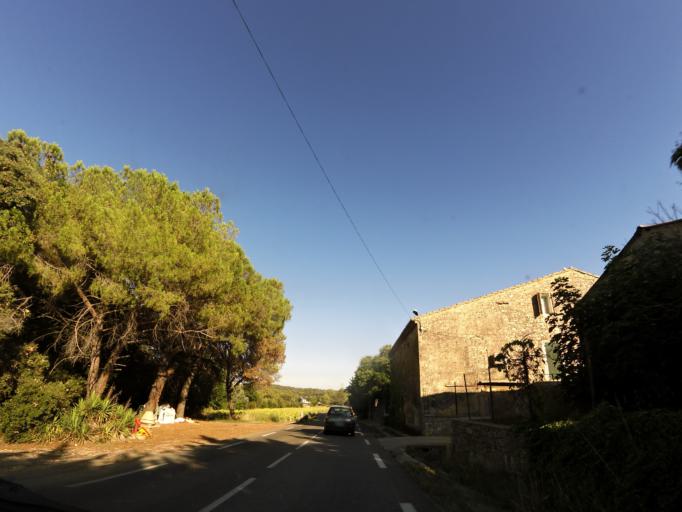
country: FR
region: Languedoc-Roussillon
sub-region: Departement du Gard
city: Sommieres
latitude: 43.8344
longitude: 4.0364
